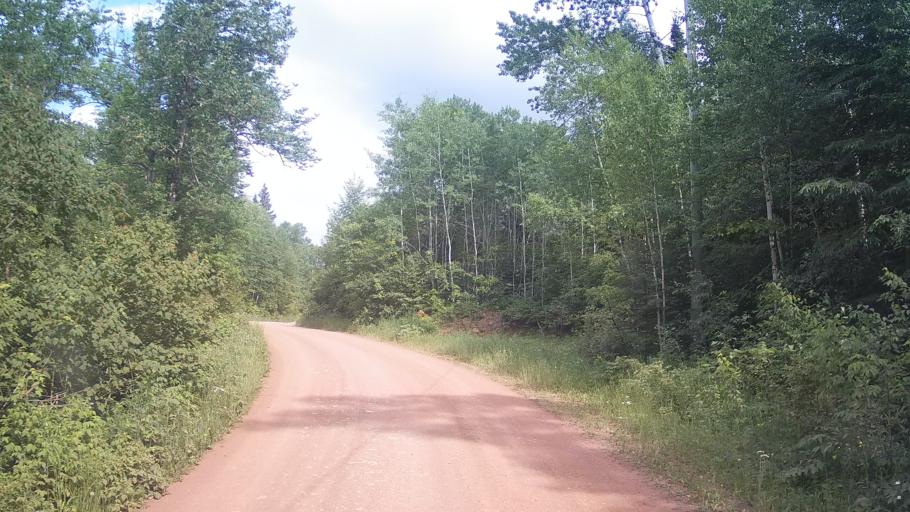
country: CA
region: Ontario
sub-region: Thunder Bay District
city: Thunder Bay
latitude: 48.6656
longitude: -88.6647
